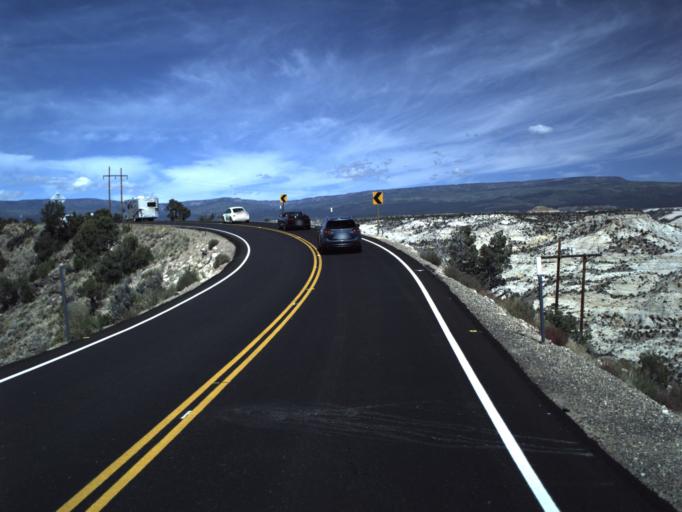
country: US
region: Utah
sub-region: Wayne County
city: Loa
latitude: 37.8383
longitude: -111.4207
